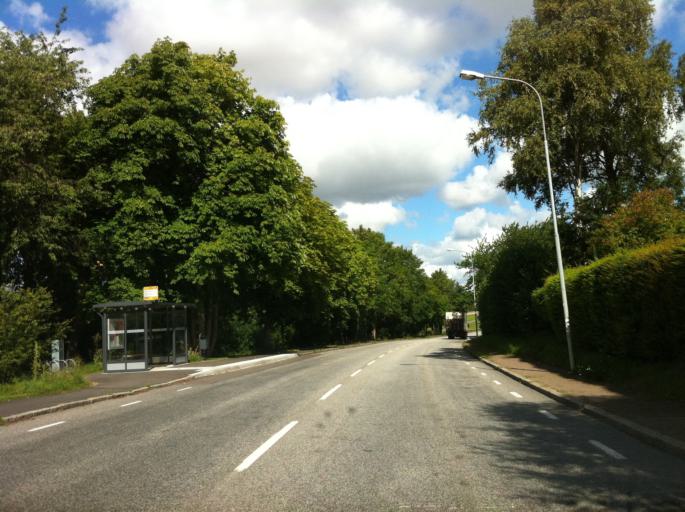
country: SE
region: Skane
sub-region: Svalovs Kommun
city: Svaloev
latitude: 55.9146
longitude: 13.1050
